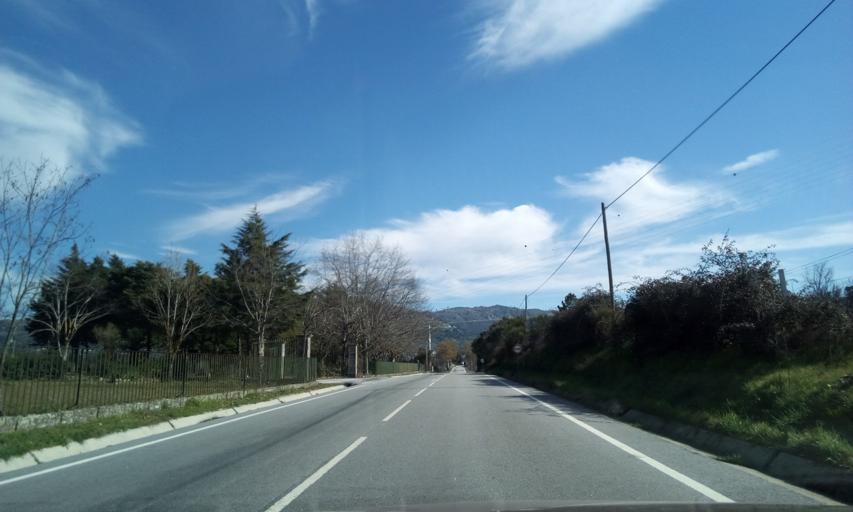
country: PT
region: Guarda
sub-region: Celorico da Beira
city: Celorico da Beira
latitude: 40.6215
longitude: -7.3163
